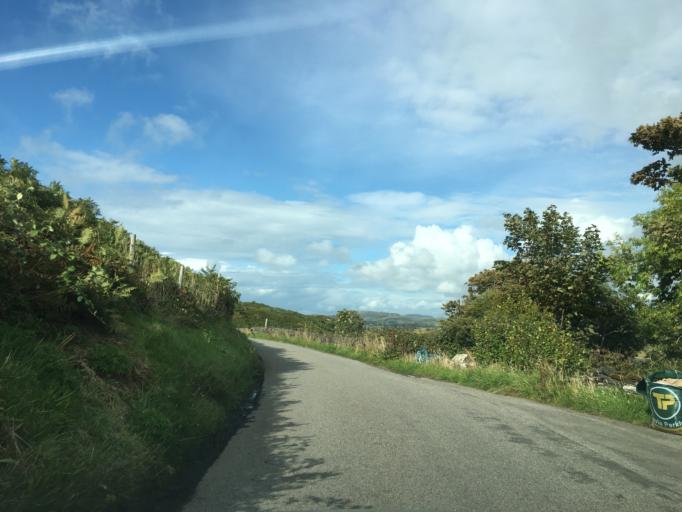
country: GB
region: Scotland
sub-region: Argyll and Bute
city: Oban
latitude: 56.2731
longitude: -5.6267
